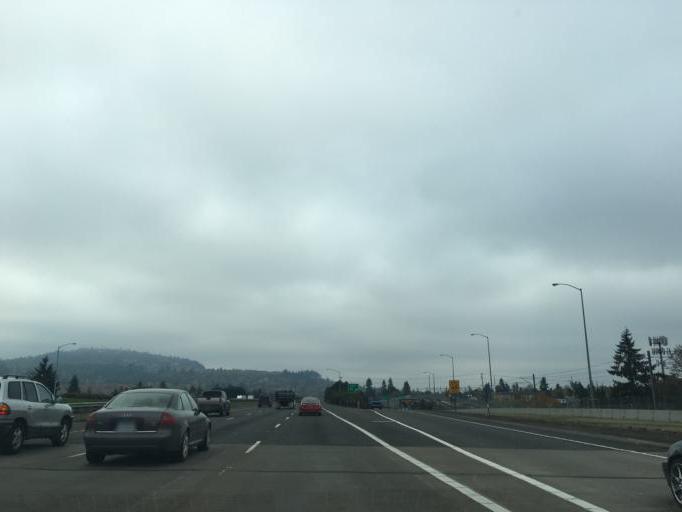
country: US
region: Oregon
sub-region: Multnomah County
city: Lents
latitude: 45.4828
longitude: -122.5662
